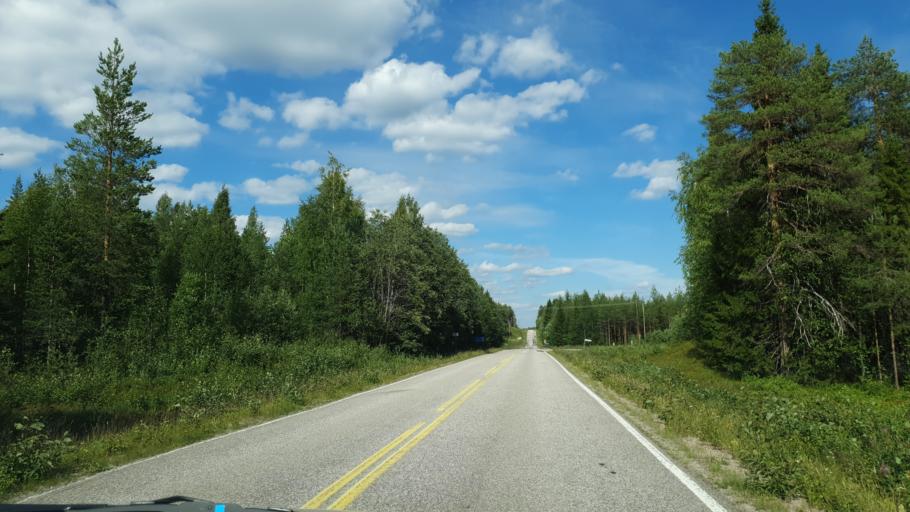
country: FI
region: Kainuu
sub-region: Kajaani
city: Sotkamo
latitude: 64.1665
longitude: 28.8546
